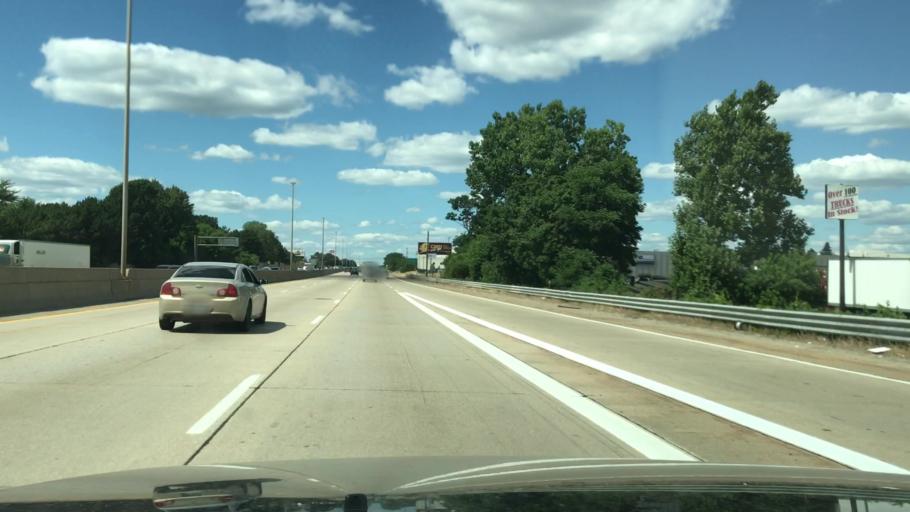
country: US
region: Michigan
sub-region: Kent County
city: Cutlerville
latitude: 42.8690
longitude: -85.6801
